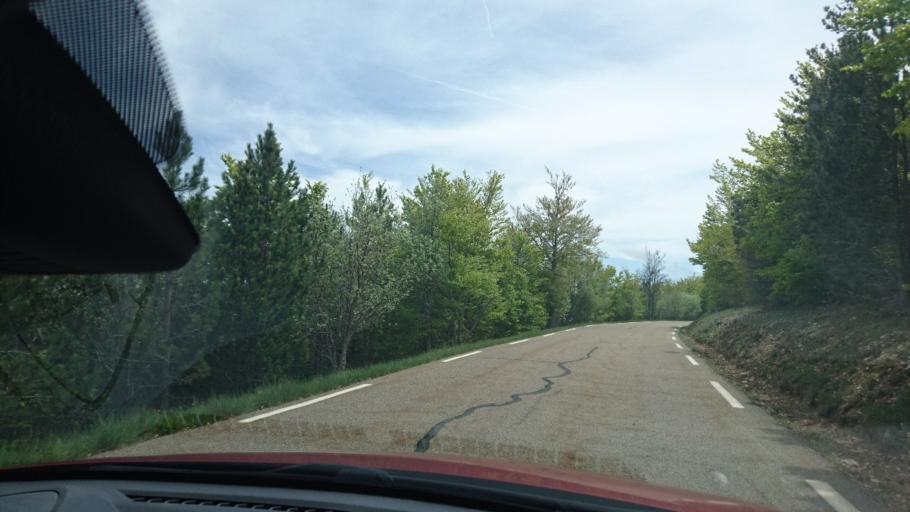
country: FR
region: Provence-Alpes-Cote d'Azur
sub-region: Departement du Vaucluse
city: Sault
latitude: 44.1431
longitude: 5.3452
